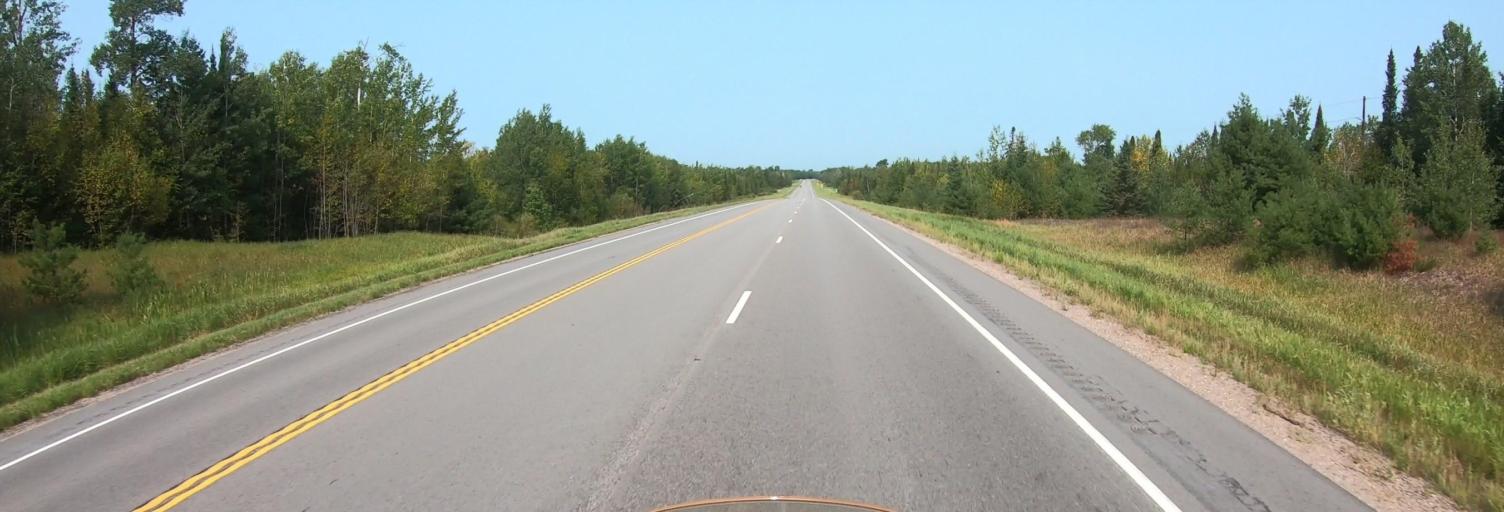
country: US
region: Minnesota
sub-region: Saint Louis County
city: Mountain Iron
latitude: 47.9158
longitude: -92.8099
